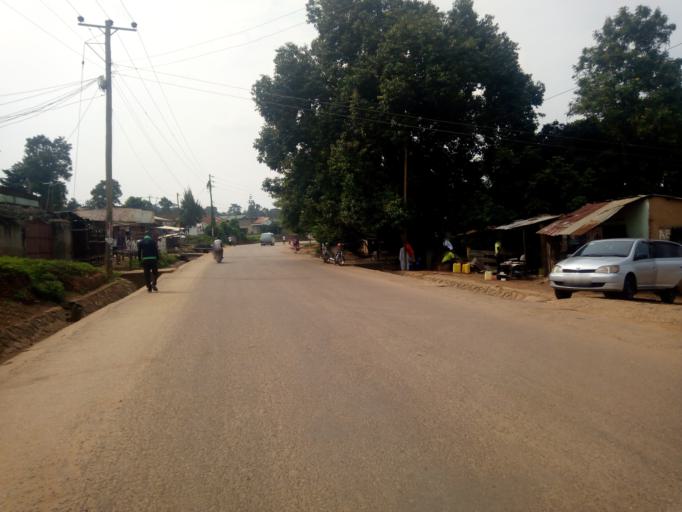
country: UG
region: Central Region
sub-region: Wakiso District
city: Kireka
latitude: 0.3042
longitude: 32.6517
